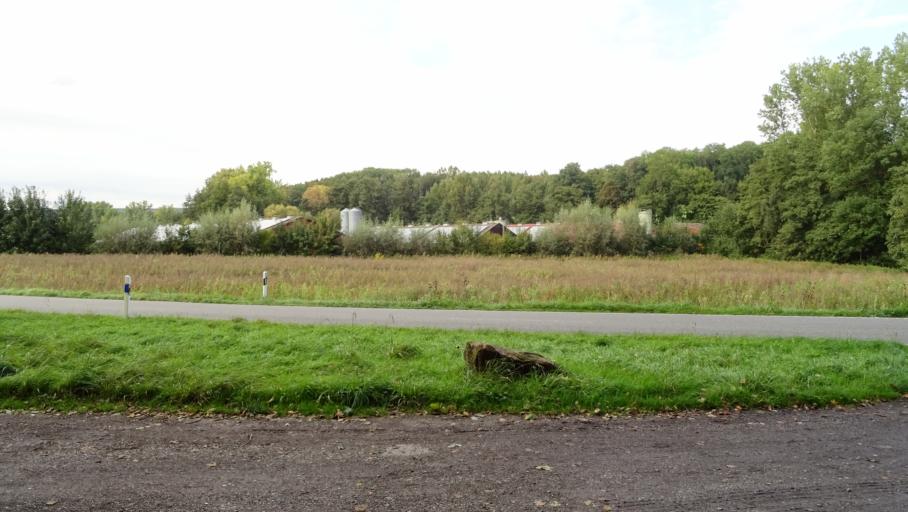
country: DE
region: Baden-Wuerttemberg
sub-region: Karlsruhe Region
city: Aglasterhausen
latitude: 49.3406
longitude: 8.9718
